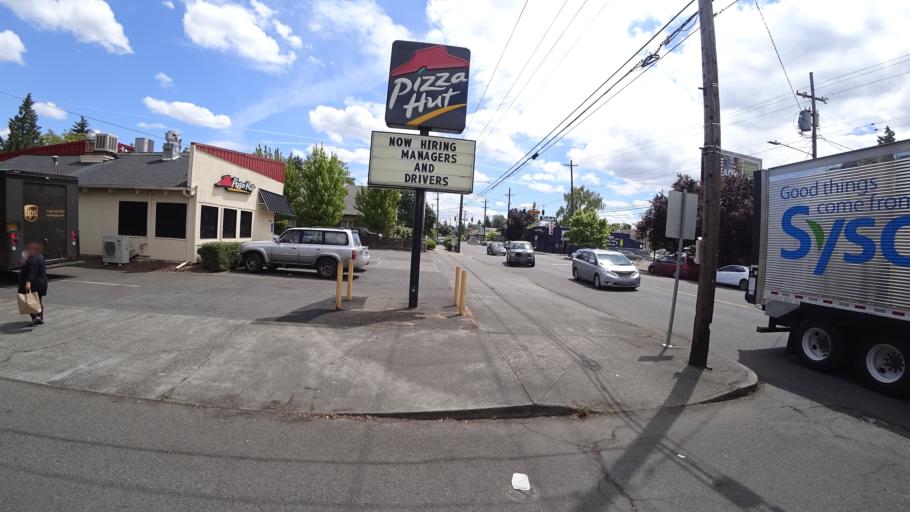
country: US
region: Oregon
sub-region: Multnomah County
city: Portland
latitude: 45.5823
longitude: -122.7233
